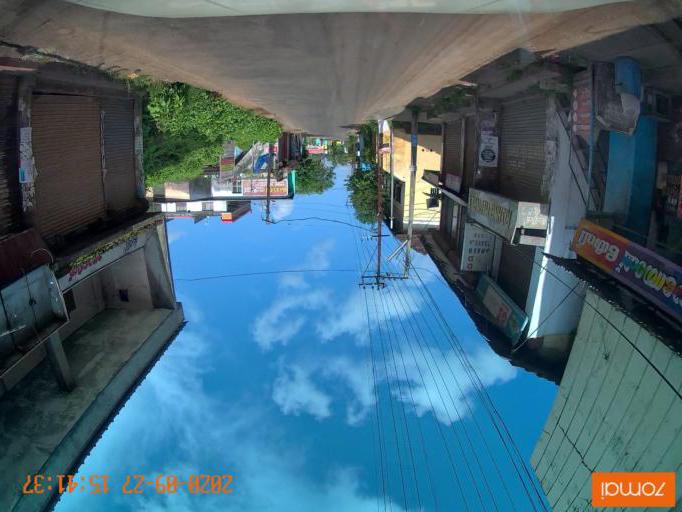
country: IN
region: Kerala
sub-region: Thrissur District
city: Thanniyam
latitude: 10.4717
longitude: 76.0965
